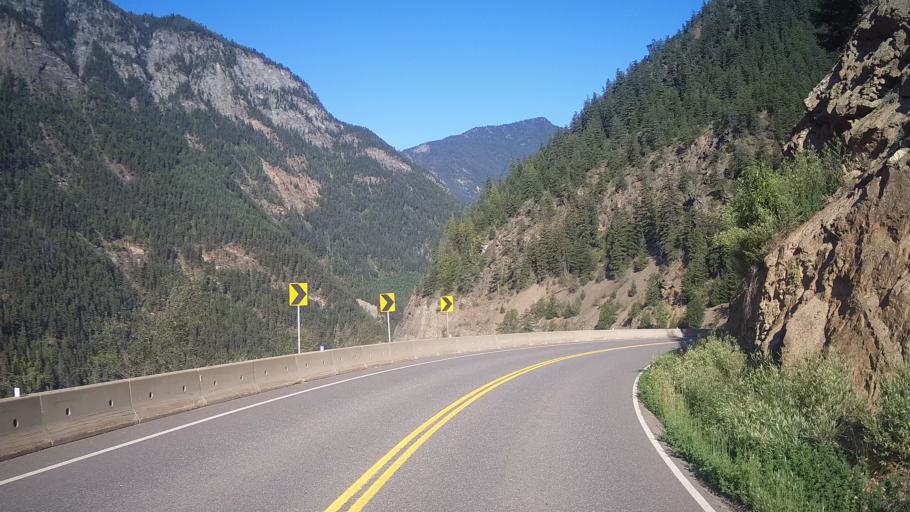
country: CA
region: British Columbia
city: Lillooet
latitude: 50.6432
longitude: -122.0294
